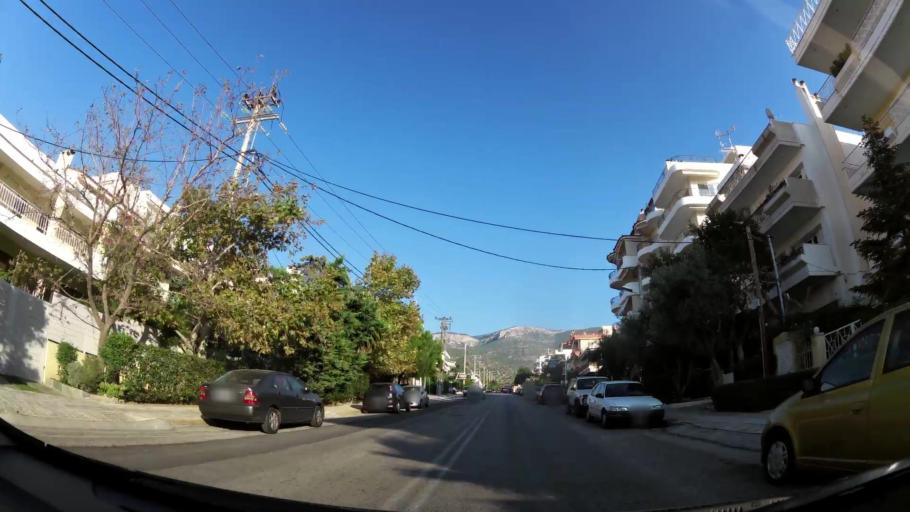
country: GR
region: Attica
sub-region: Nomarchia Athinas
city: Argyroupoli
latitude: 37.8905
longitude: 23.7738
